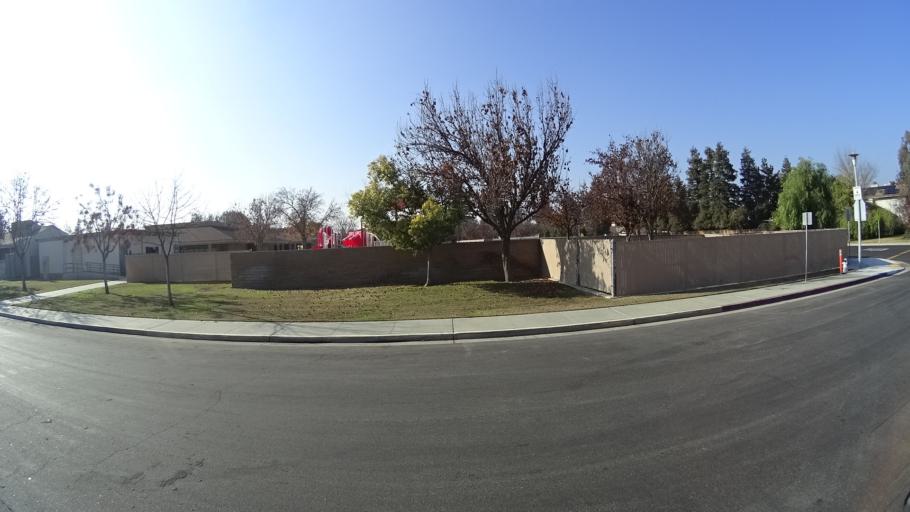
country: US
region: California
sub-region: Kern County
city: Greenacres
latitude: 35.3299
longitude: -119.1060
